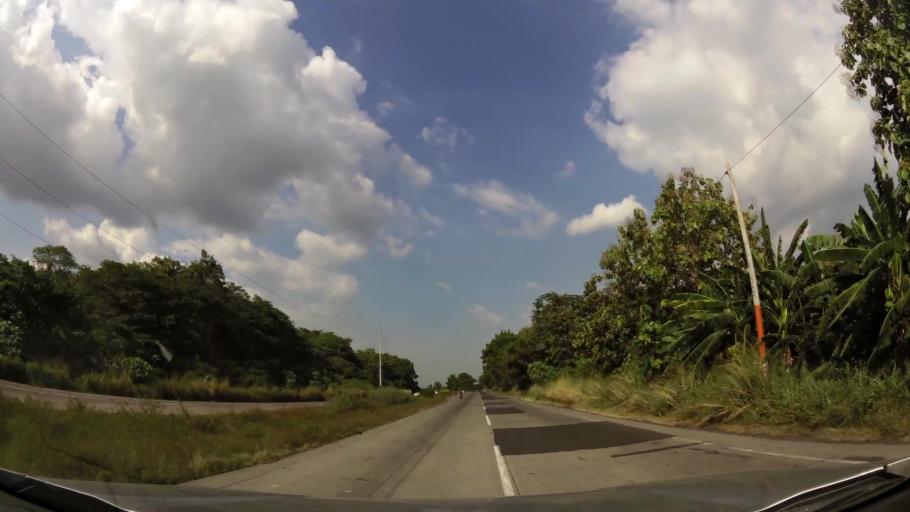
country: GT
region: Escuintla
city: Puerto San Jose
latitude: 14.0430
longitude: -90.7783
